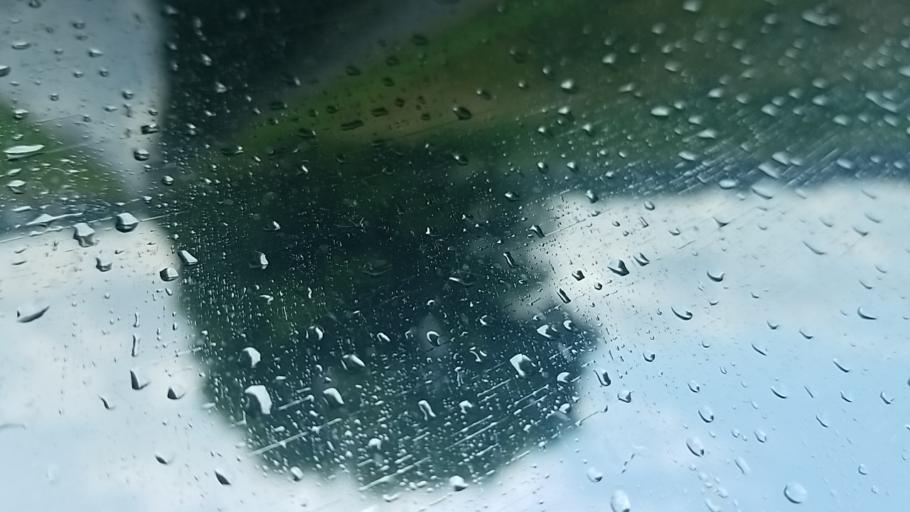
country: US
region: Ohio
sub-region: Lorain County
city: Lagrange
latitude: 41.2524
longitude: -82.0865
